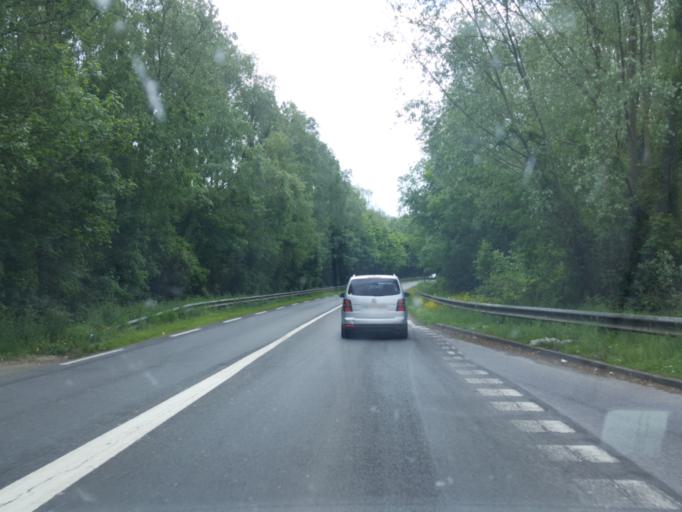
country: FR
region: Picardie
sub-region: Departement de l'Oise
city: Allonne
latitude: 49.4079
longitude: 2.1235
